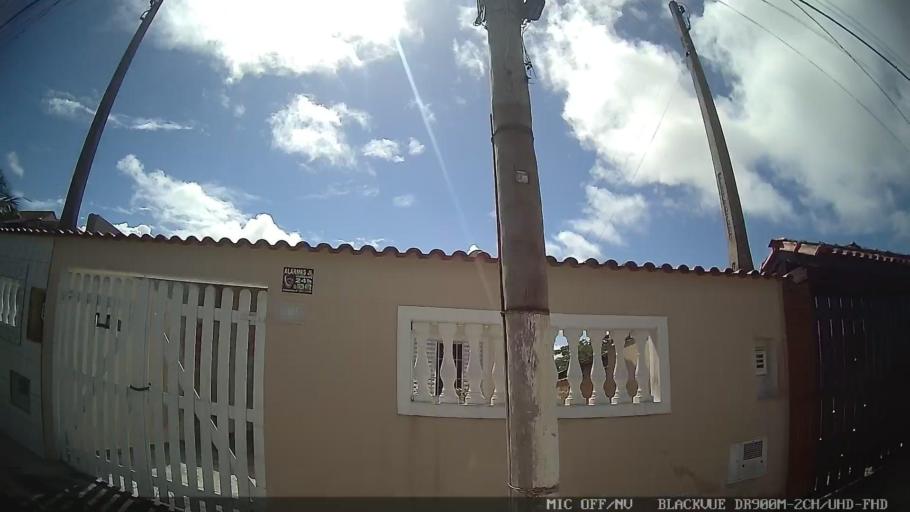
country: BR
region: Sao Paulo
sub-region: Itanhaem
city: Itanhaem
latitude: -24.2214
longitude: -46.8611
